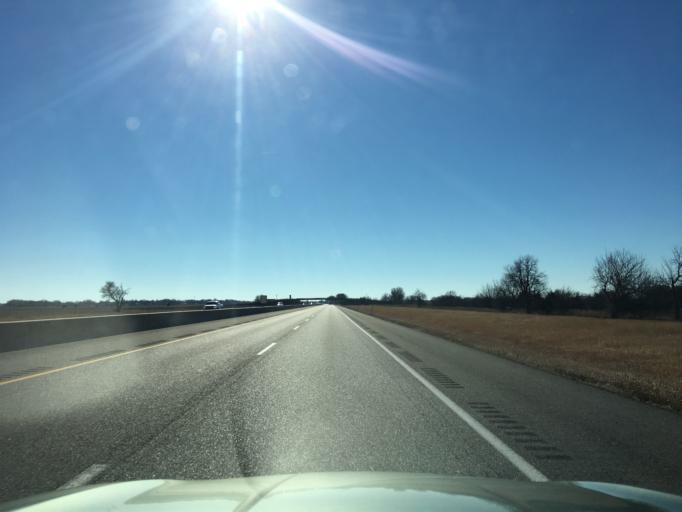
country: US
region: Kansas
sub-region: Sumner County
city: Belle Plaine
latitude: 37.4556
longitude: -97.3225
